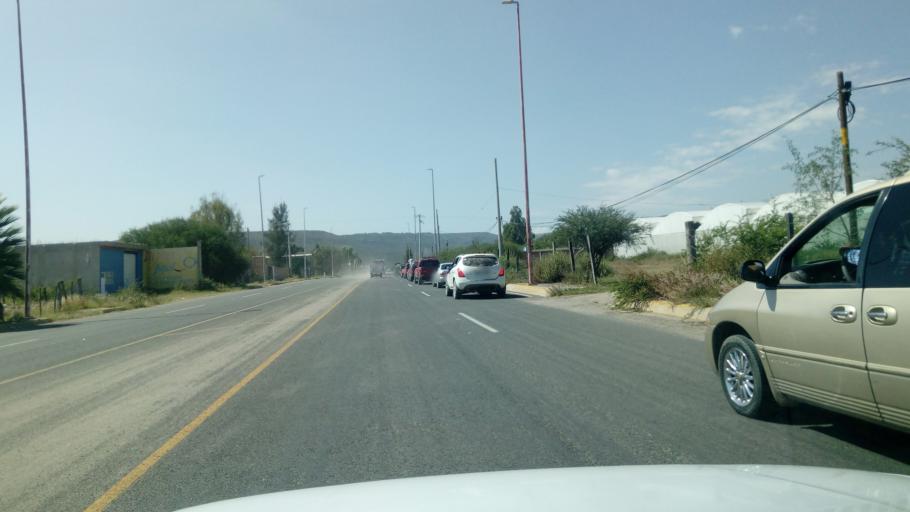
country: MX
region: Durango
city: Victoria de Durango
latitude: 23.9723
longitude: -104.6989
